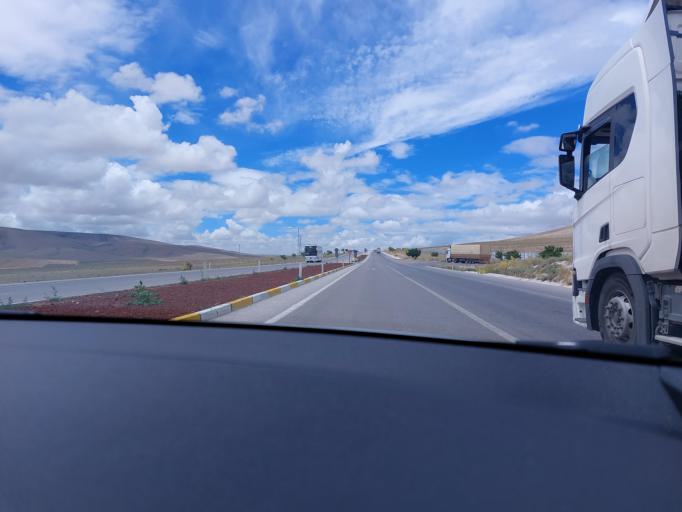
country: TR
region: Konya
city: Obruk
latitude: 38.0612
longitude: 33.0446
